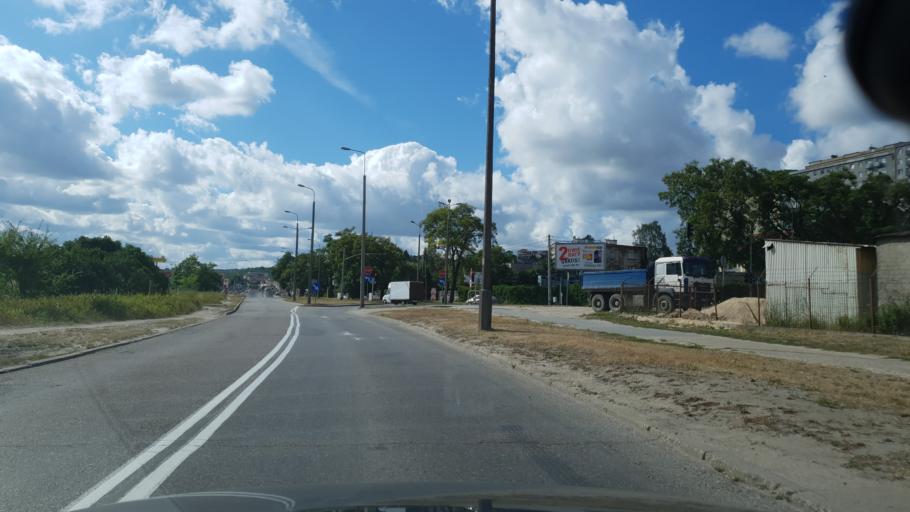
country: PL
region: Pomeranian Voivodeship
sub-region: Gdynia
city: Gdynia
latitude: 54.5481
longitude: 18.5177
